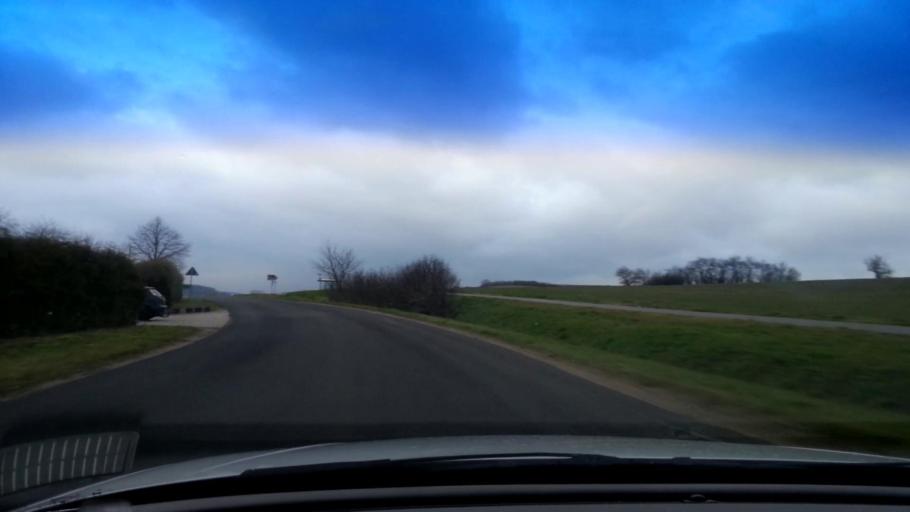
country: DE
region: Bavaria
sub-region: Upper Franconia
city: Walsdorf
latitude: 49.8311
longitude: 10.7801
